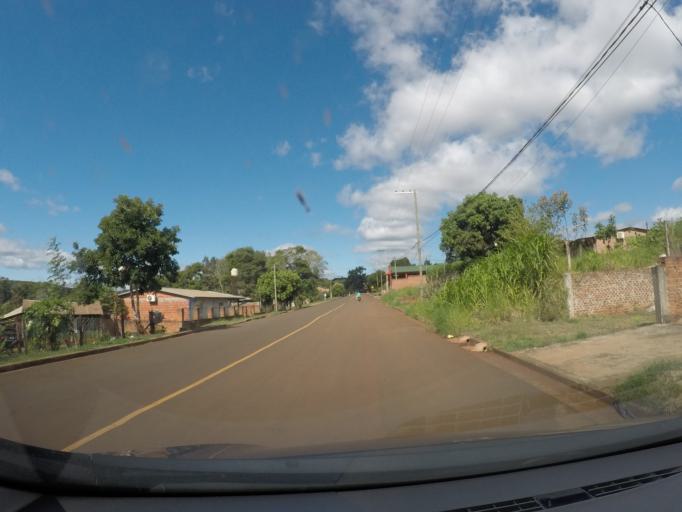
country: AR
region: Misiones
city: Puerto Rico
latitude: -26.8002
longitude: -55.0136
